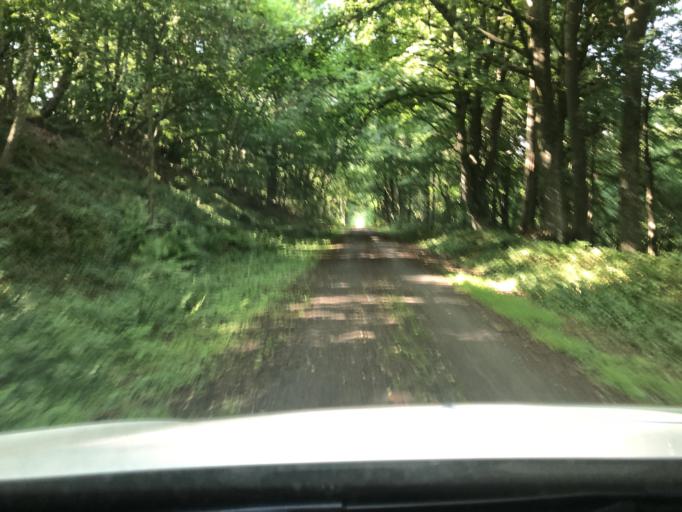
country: SE
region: Skane
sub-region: Kristianstads Kommun
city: Degeberga
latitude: 55.8056
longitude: 14.1365
